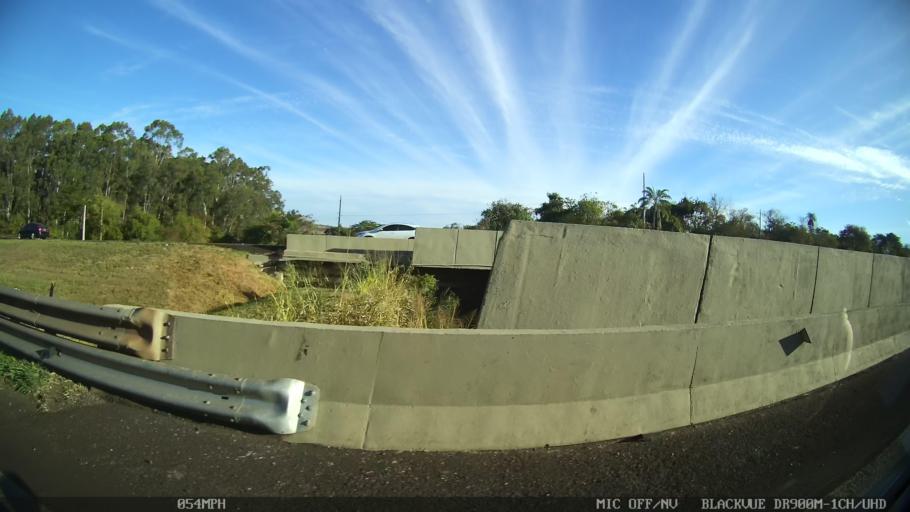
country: BR
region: Sao Paulo
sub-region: Sao Jose Do Rio Preto
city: Sao Jose do Rio Preto
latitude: -20.8169
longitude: -49.4381
